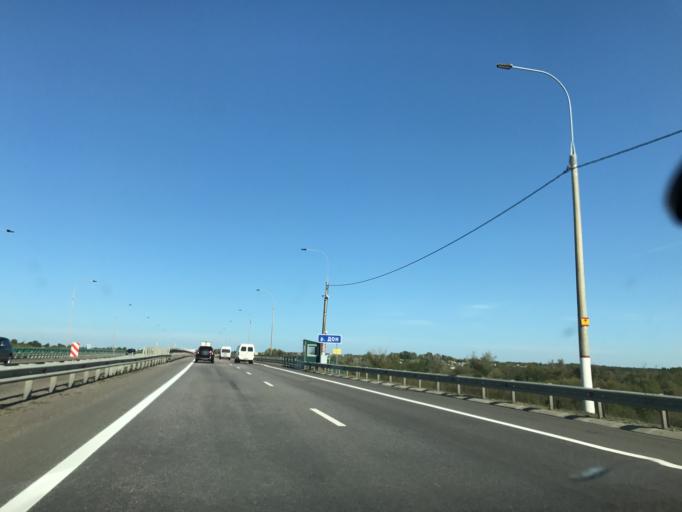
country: RU
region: Voronezj
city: Verkhniy Mamon
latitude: 50.1661
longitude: 40.4312
